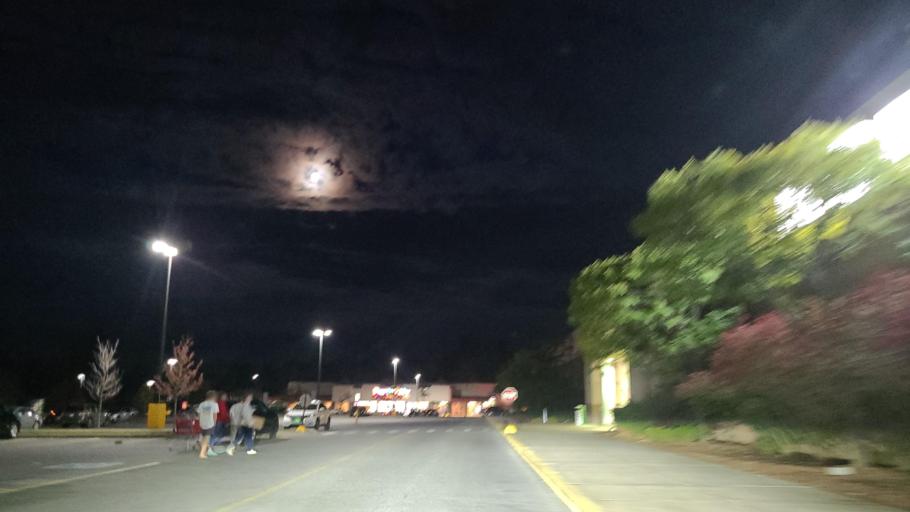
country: US
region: Vermont
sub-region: Chittenden County
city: South Burlington
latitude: 44.4640
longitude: -73.1836
